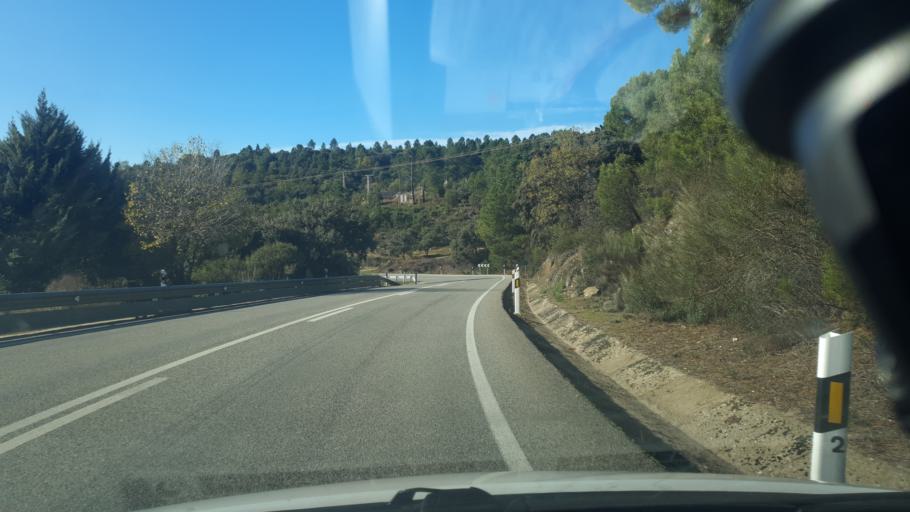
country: ES
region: Castille and Leon
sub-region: Provincia de Avila
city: Arenas de San Pedro
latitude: 40.1963
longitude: -5.0459
